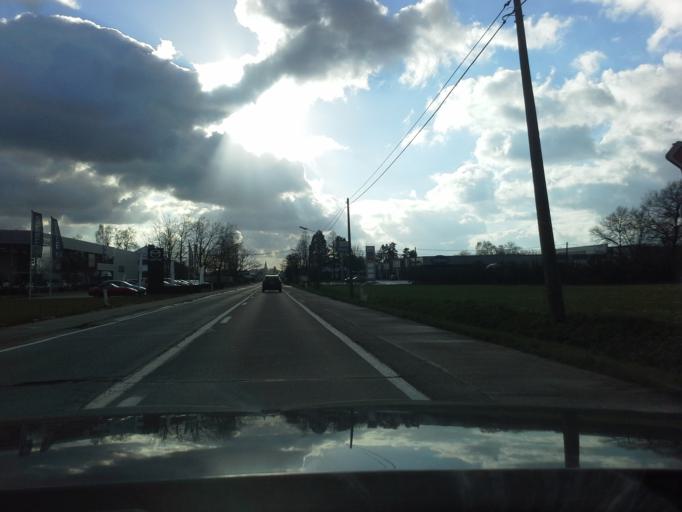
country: BE
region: Flanders
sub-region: Provincie Antwerpen
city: Meerhout
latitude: 51.1445
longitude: 5.0875
